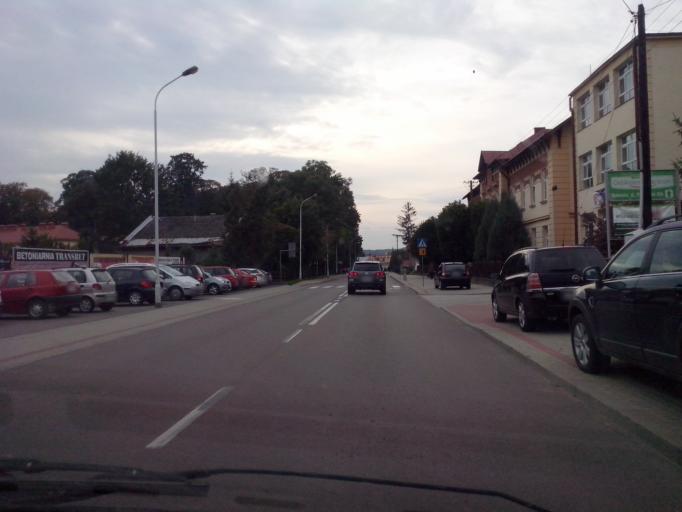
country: PL
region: Subcarpathian Voivodeship
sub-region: Powiat przemyski
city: Dubiecko
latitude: 49.8235
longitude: 22.3986
